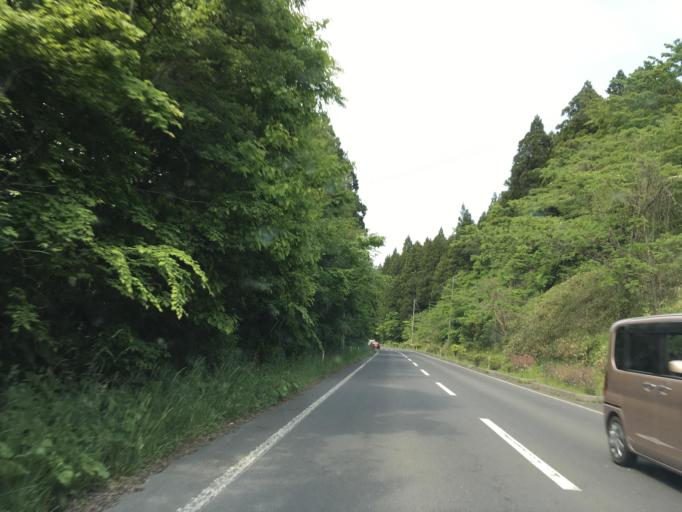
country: JP
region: Iwate
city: Ofunato
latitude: 38.8685
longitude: 141.5357
